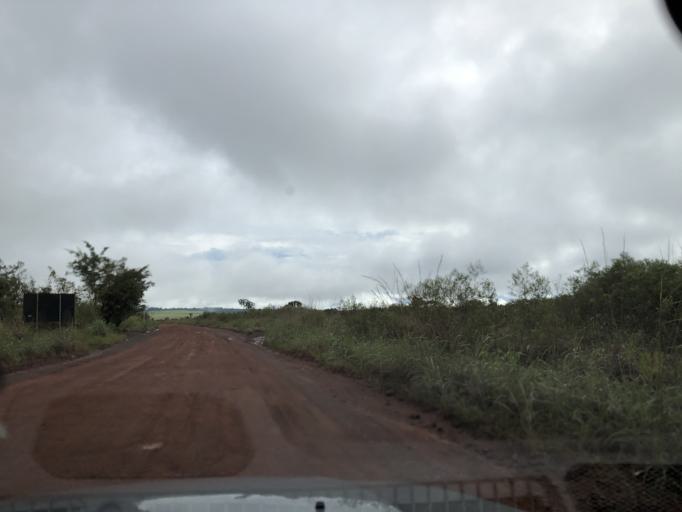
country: BR
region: Federal District
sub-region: Brasilia
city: Brasilia
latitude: -15.6124
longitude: -48.0450
